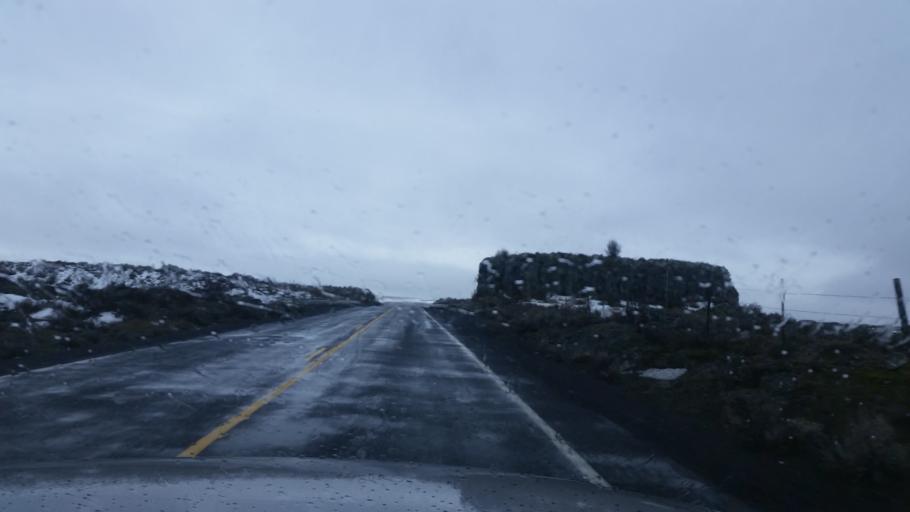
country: US
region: Washington
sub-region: Lincoln County
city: Davenport
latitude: 47.3679
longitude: -118.1135
